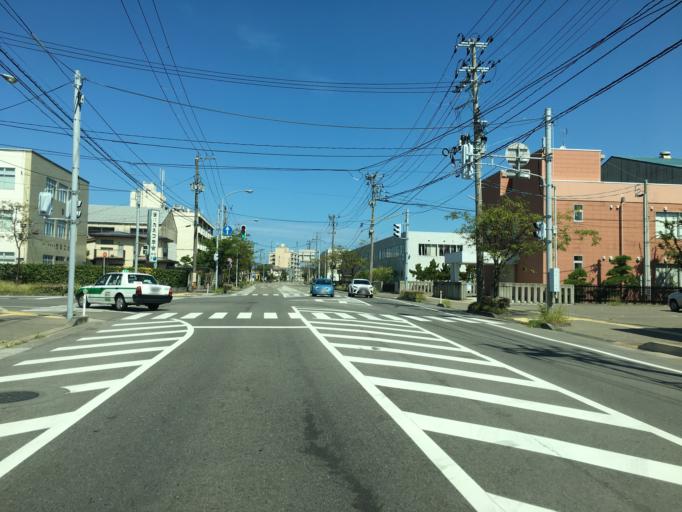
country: JP
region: Niigata
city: Niigata-shi
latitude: 37.9357
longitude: 139.0570
